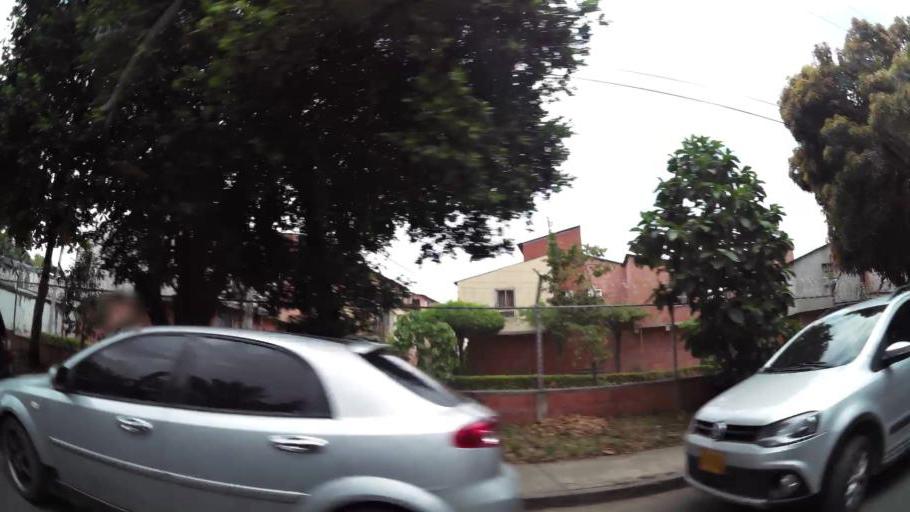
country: CO
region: Valle del Cauca
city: Cali
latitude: 3.4658
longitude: -76.4976
